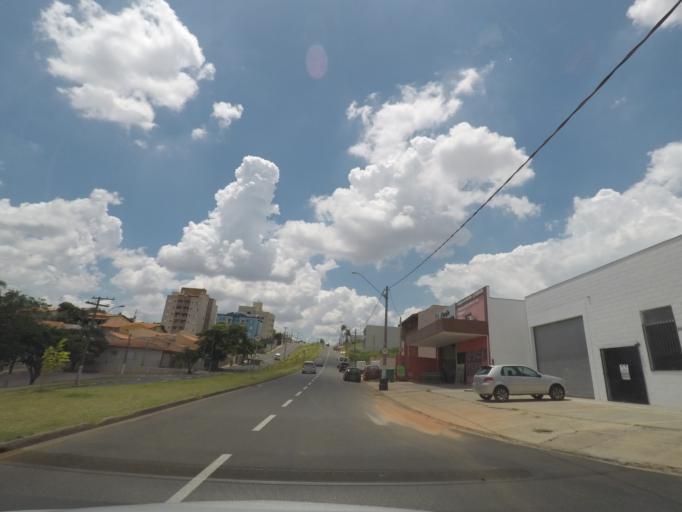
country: BR
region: Sao Paulo
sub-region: Valinhos
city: Valinhos
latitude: -22.9849
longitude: -46.9965
